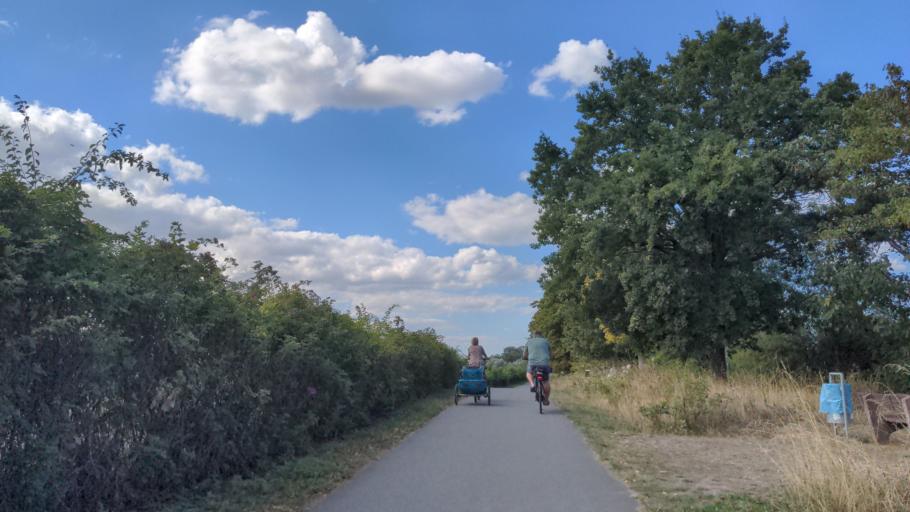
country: DE
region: Mecklenburg-Vorpommern
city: Wismar
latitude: 53.9152
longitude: 11.4160
